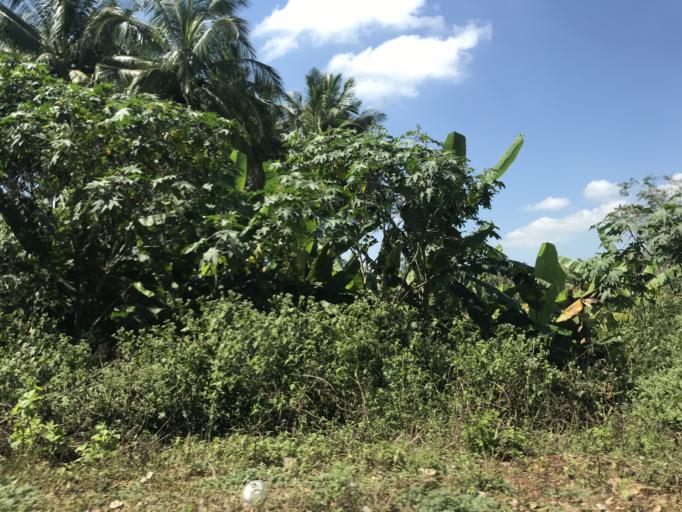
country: IN
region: Karnataka
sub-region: Mysore
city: Heggadadevankote
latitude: 12.1143
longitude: 76.3123
